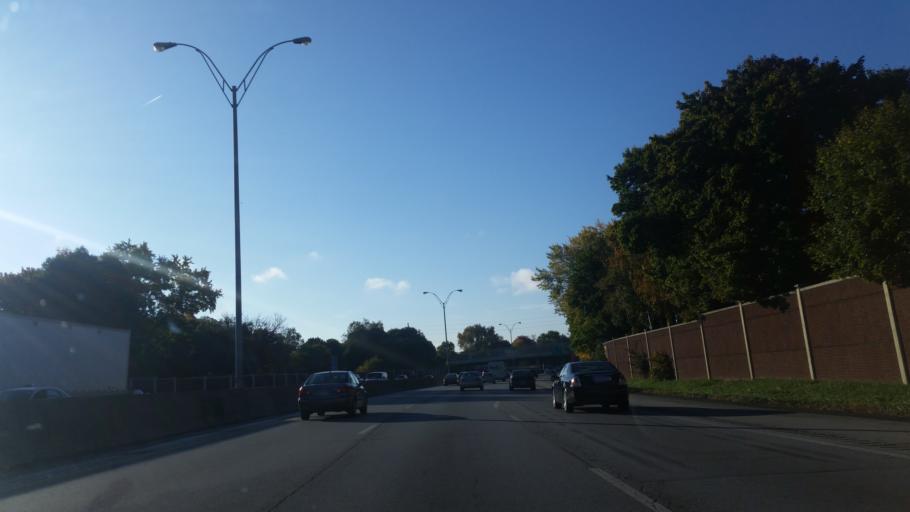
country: US
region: Ohio
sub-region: Summit County
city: Akron
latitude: 41.0802
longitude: -81.5748
